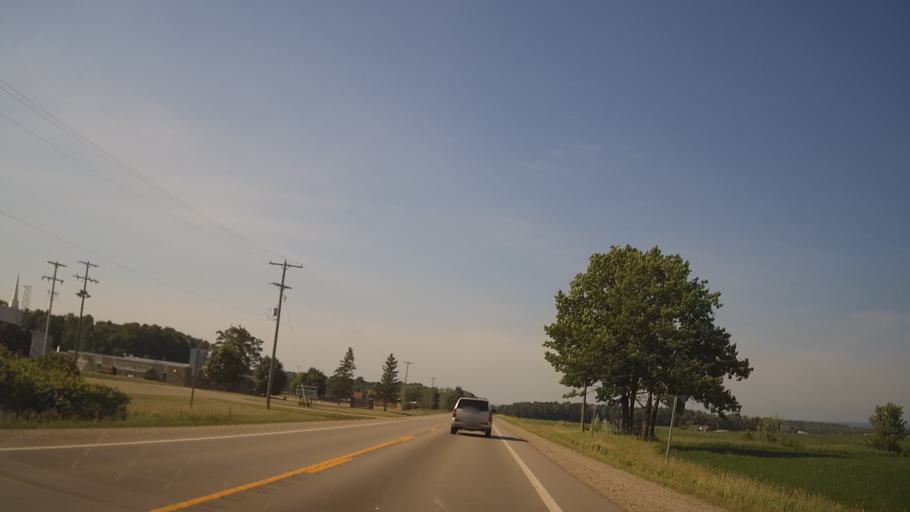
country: US
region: Michigan
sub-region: Ogemaw County
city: West Branch
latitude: 44.3050
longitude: -84.1258
